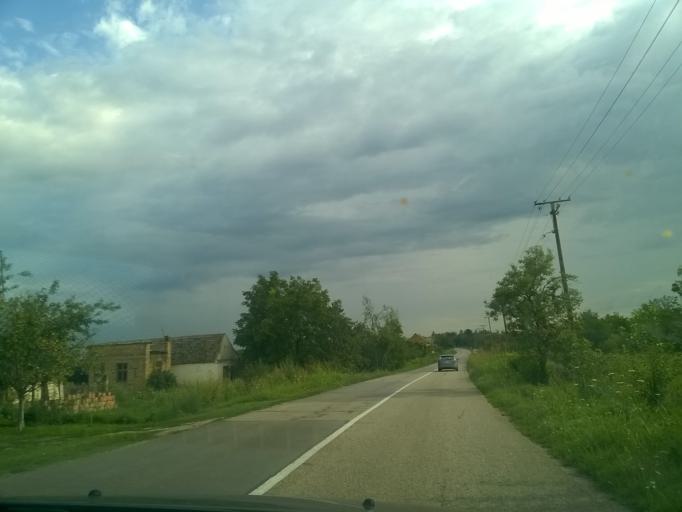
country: RS
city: Uzdin
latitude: 45.1978
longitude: 20.6209
